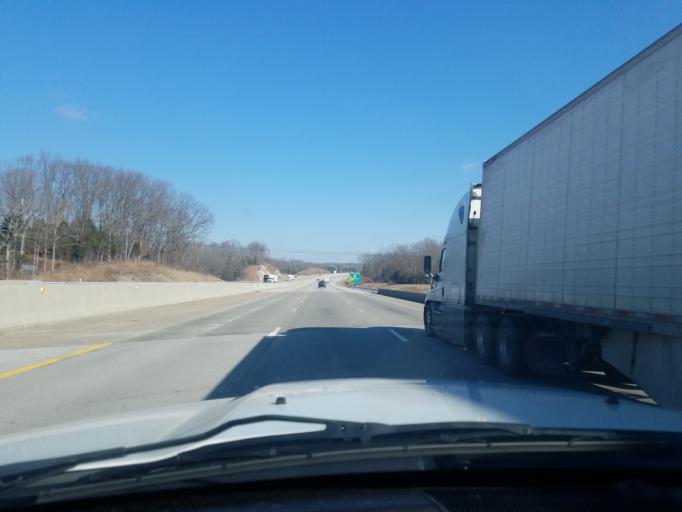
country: US
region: Kentucky
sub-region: Barren County
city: Cave City
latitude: 37.0909
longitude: -86.0600
